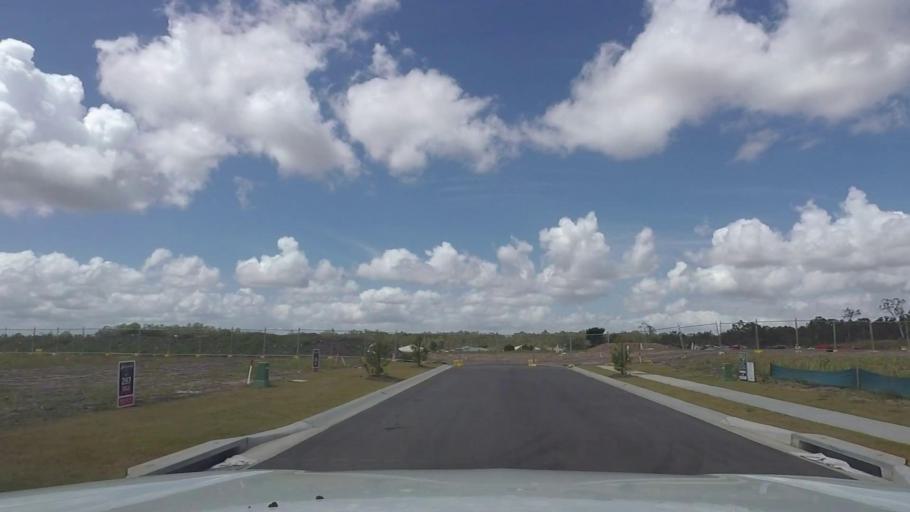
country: AU
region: Queensland
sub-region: Logan
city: Logan Reserve
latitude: -27.7091
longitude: 153.0797
